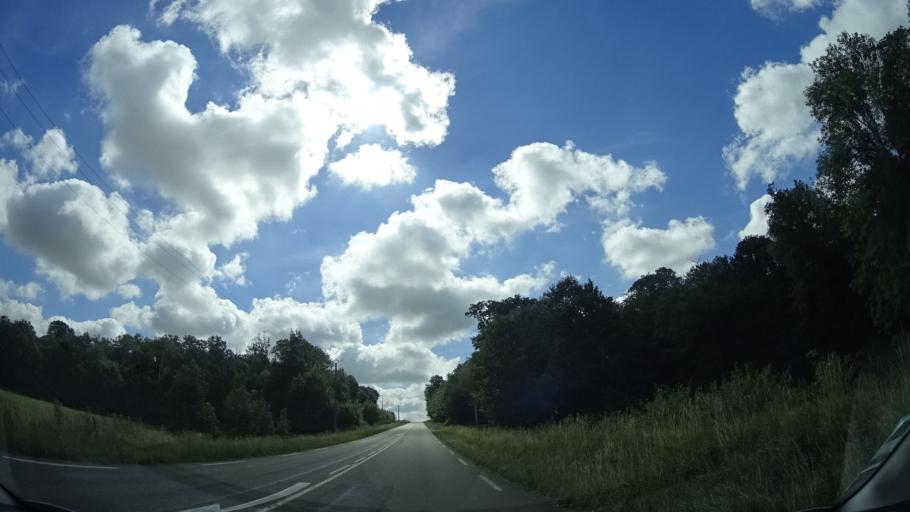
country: FR
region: Pays de la Loire
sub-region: Departement de la Mayenne
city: Entrammes
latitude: 48.0066
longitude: -0.6567
